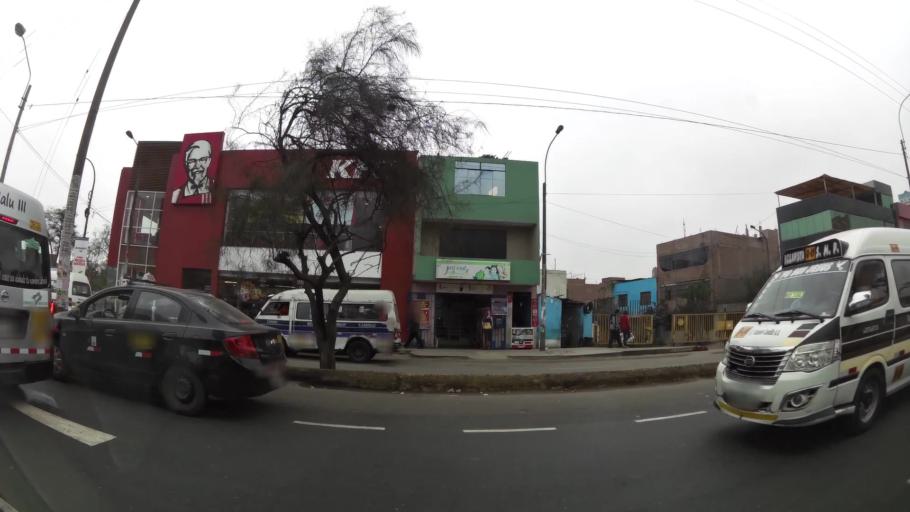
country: PE
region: Lima
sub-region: Lima
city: Independencia
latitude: -11.9335
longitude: -77.0466
